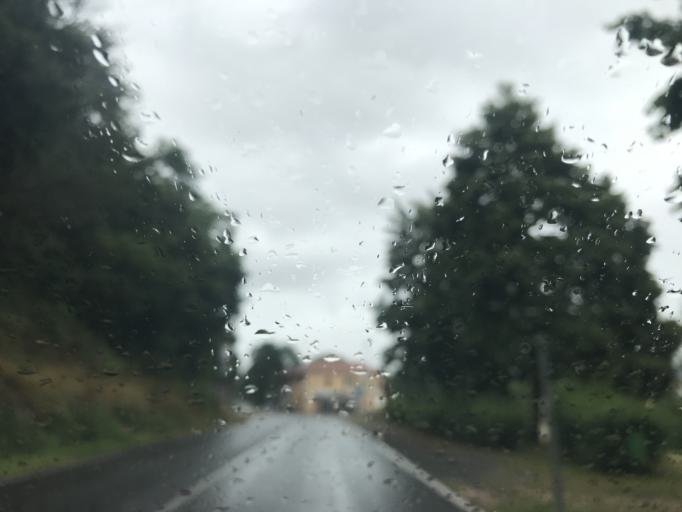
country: FR
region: Auvergne
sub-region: Departement du Puy-de-Dome
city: Ambert
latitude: 45.5498
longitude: 3.7299
